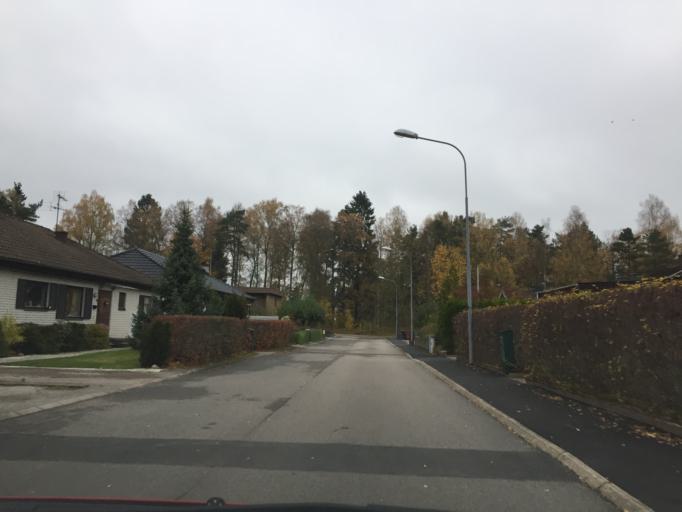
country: SE
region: Vaestra Goetaland
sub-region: Trollhattan
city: Trollhattan
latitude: 58.2573
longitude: 12.2903
